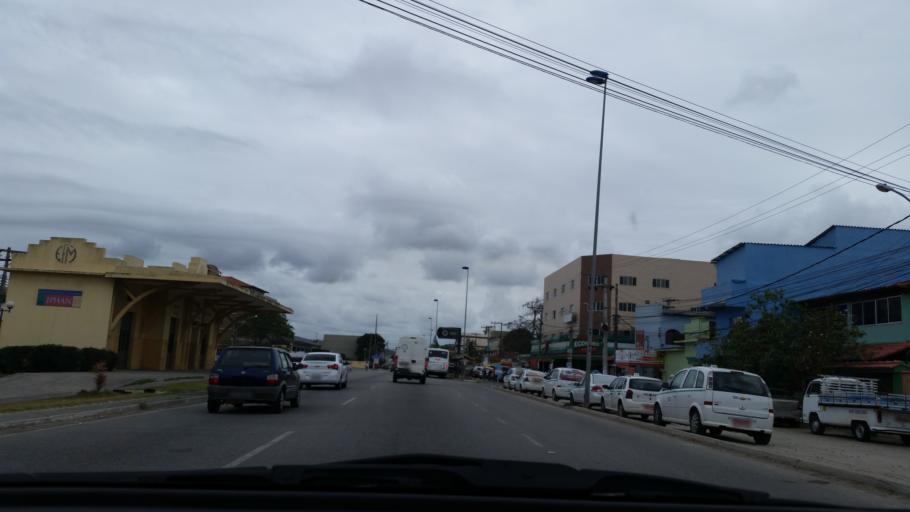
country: BR
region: Rio de Janeiro
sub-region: Sao Pedro Da Aldeia
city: Sao Pedro da Aldeia
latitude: -22.8337
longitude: -42.1029
